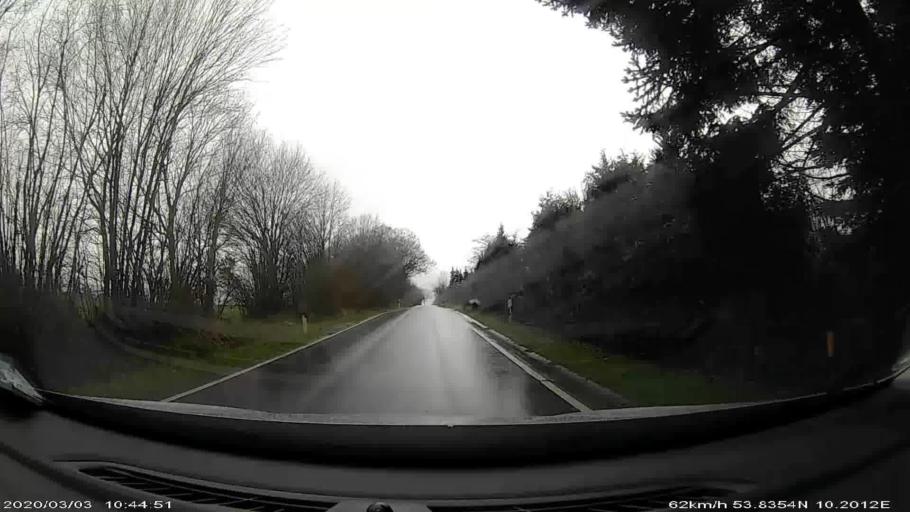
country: DE
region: Schleswig-Holstein
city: Seth
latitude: 53.8365
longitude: 10.1964
